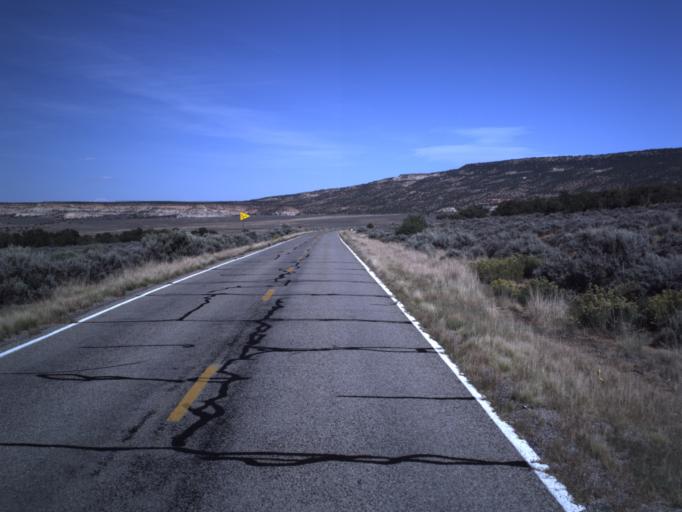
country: US
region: Utah
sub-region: San Juan County
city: Monticello
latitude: 38.0037
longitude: -109.4560
